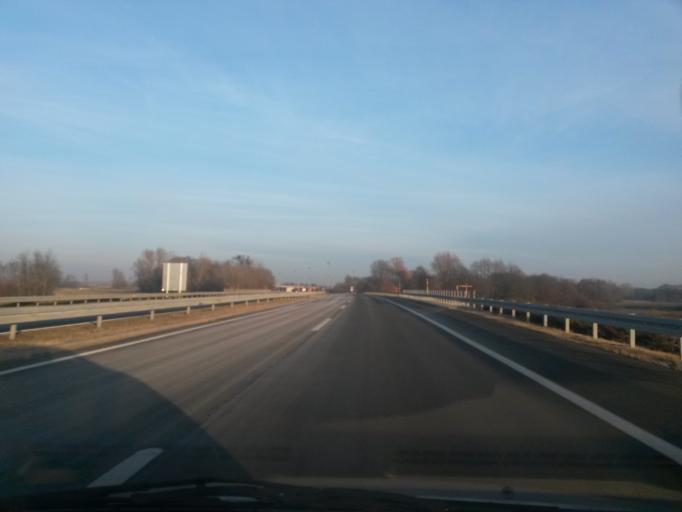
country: HR
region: Varazdinska
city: Jalzabet
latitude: 46.2841
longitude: 16.4744
